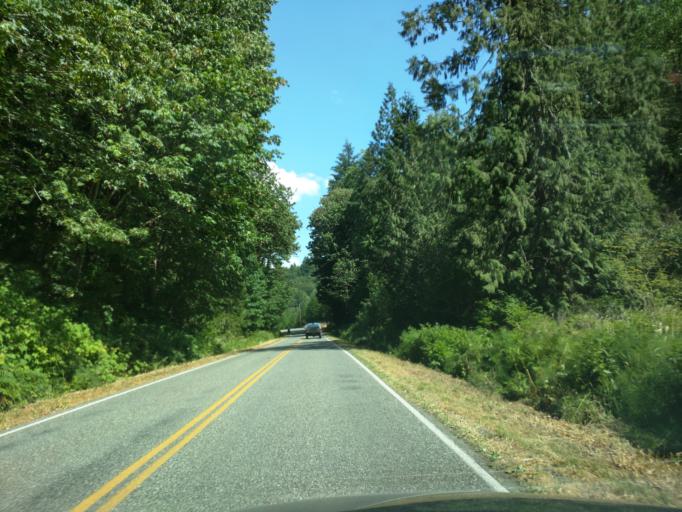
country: US
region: Washington
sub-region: Whatcom County
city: Peaceful Valley
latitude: 48.9634
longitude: -122.1783
